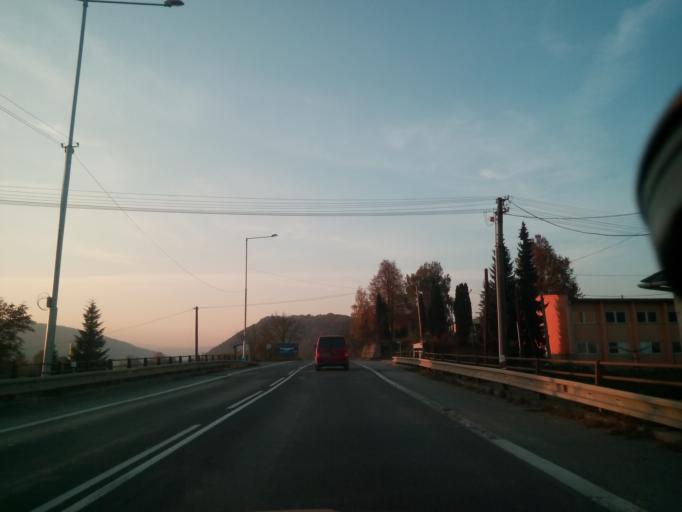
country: SK
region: Presovsky
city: Sabinov
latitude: 49.0062
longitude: 21.0703
